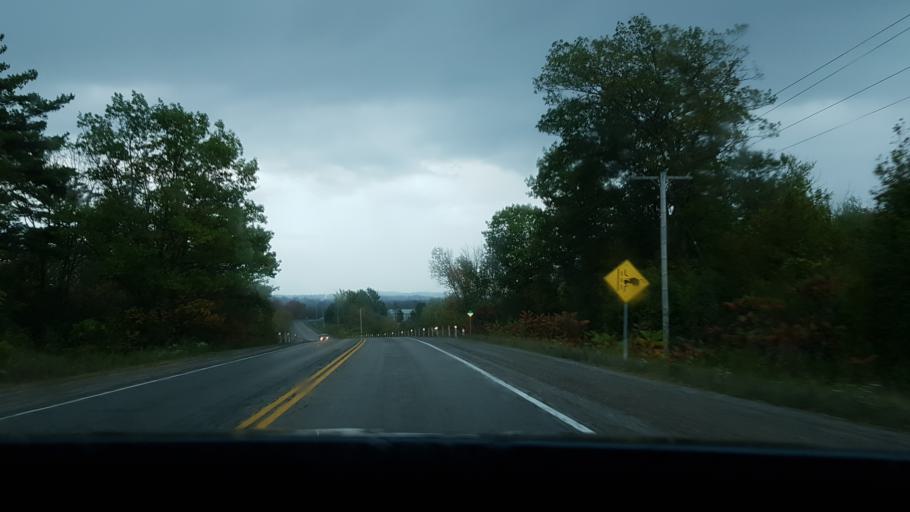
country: CA
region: Ontario
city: Omemee
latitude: 44.3622
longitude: -78.5428
